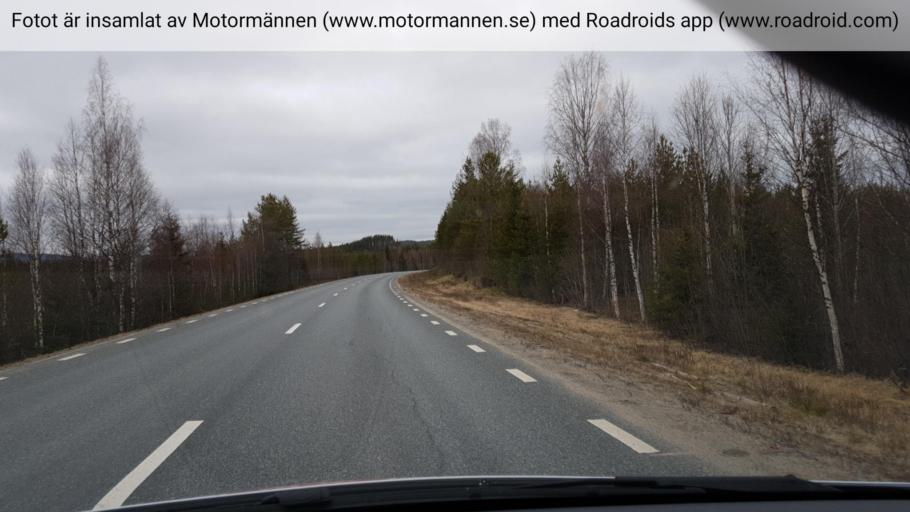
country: SE
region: Vaesternorrland
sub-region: OErnskoeldsviks Kommun
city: Ornskoldsvik
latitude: 63.6977
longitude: 18.5100
